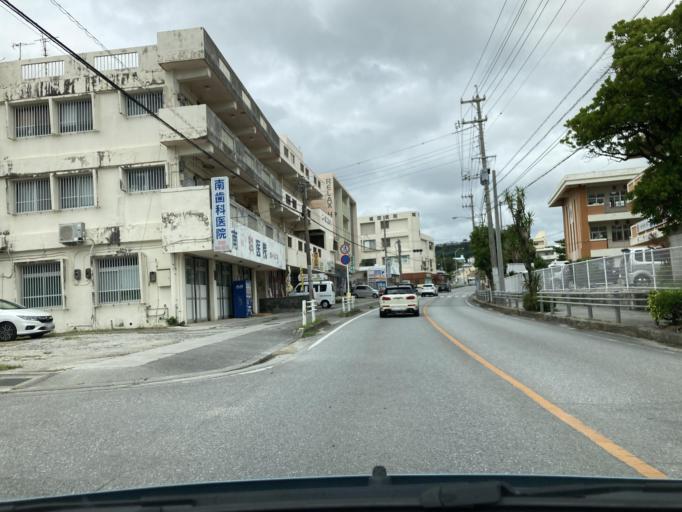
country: JP
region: Okinawa
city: Ginowan
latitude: 26.2280
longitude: 127.7546
